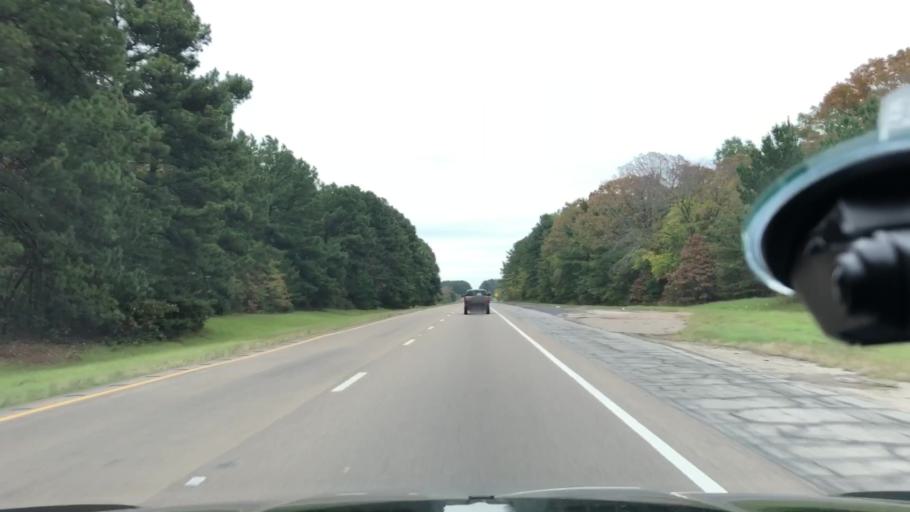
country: US
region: Texas
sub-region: Morris County
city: Naples
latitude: 33.3059
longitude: -94.7025
